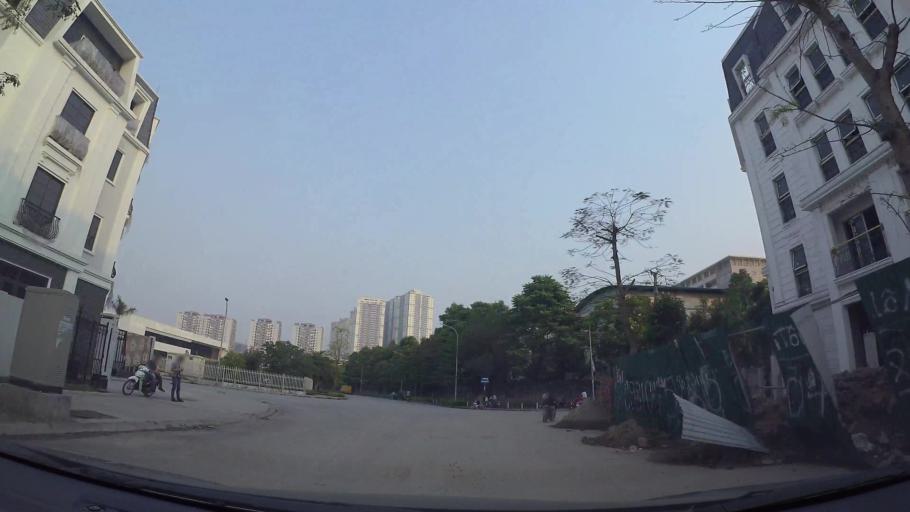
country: VN
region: Ha Noi
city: Thanh Xuan
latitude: 20.9775
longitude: 105.8155
